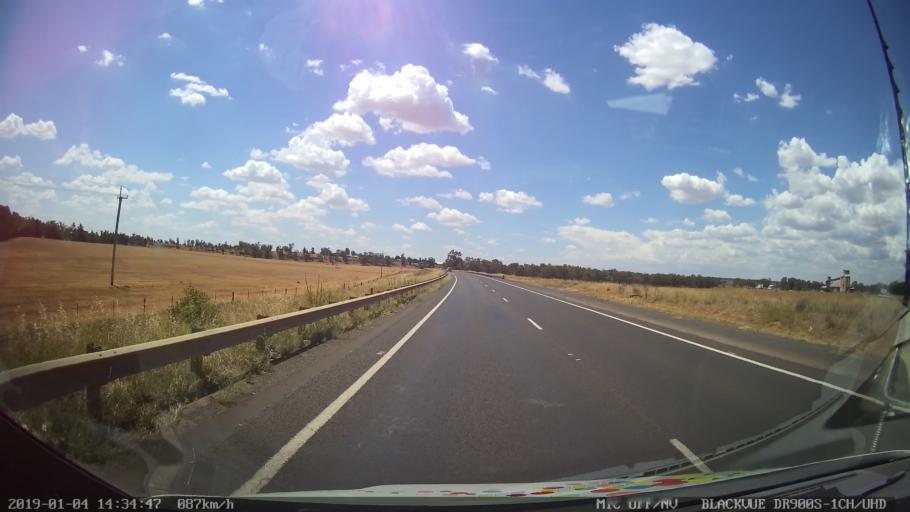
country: AU
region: New South Wales
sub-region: Dubbo Municipality
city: Dubbo
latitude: -32.1941
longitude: 148.6211
